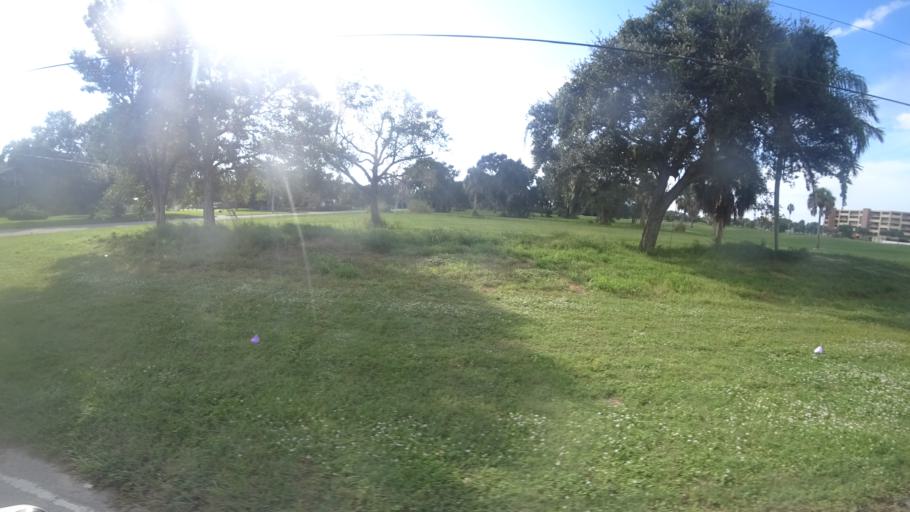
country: US
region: Florida
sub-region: Manatee County
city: Palmetto
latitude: 27.5326
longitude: -82.5811
